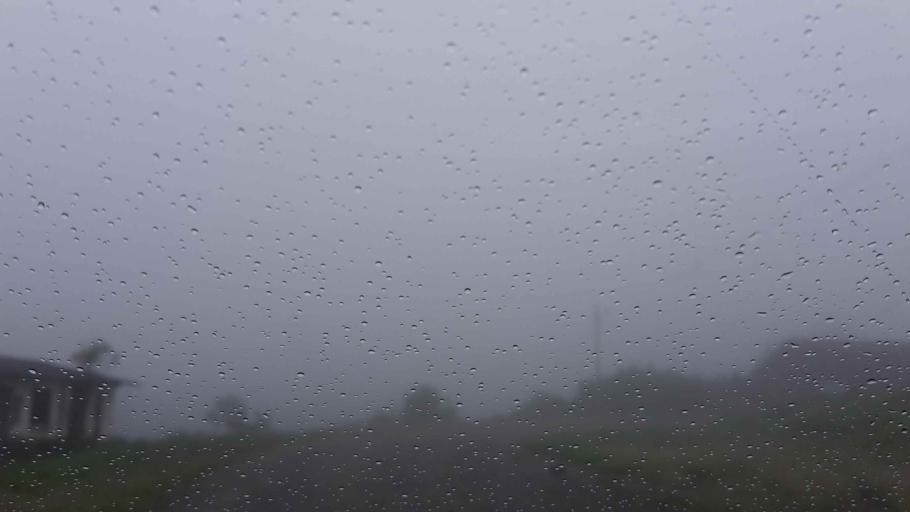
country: BO
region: Cochabamba
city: Colomi
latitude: -17.0847
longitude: -65.9991
